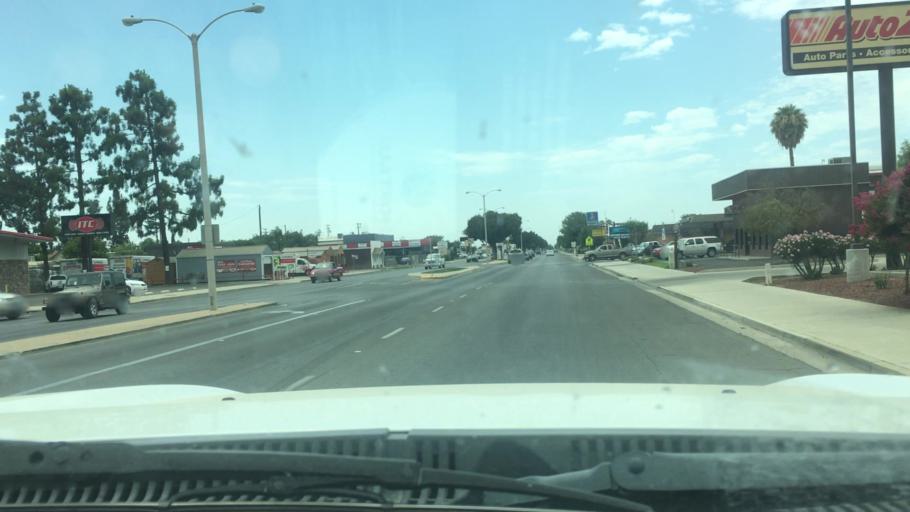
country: US
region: California
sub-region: Tulare County
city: Porterville
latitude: 36.0660
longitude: -119.0424
